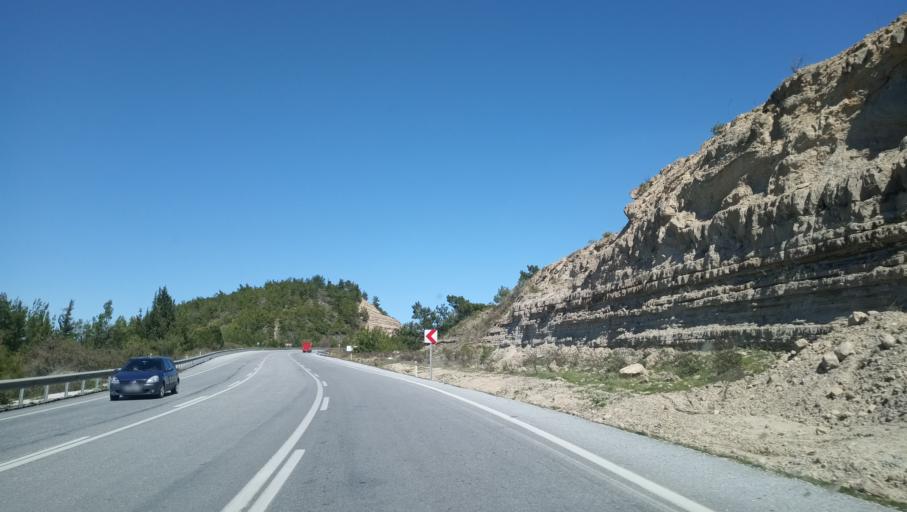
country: TR
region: Antalya
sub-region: Manavgat
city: Kizilagac
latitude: 36.7440
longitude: 31.6178
